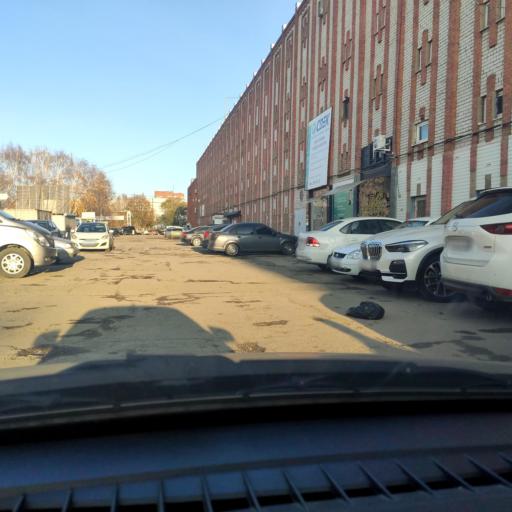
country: RU
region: Samara
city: Tol'yatti
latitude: 53.5418
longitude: 49.3120
